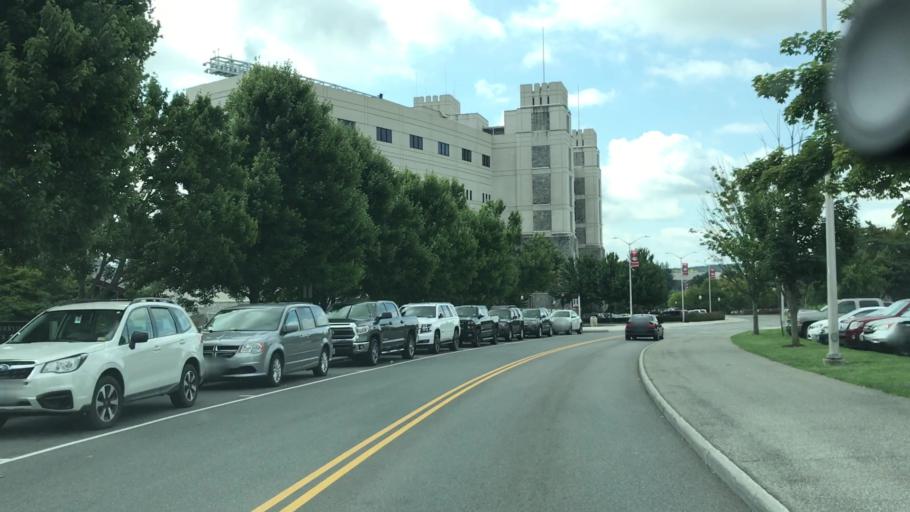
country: US
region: Virginia
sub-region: Montgomery County
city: Blacksburg
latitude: 37.2216
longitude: -80.4196
